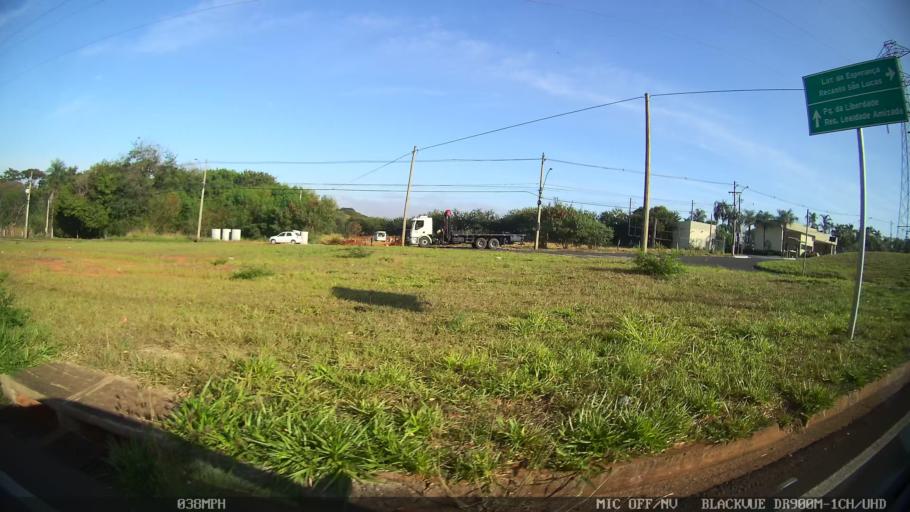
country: BR
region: Sao Paulo
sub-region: Sao Jose Do Rio Preto
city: Sao Jose do Rio Preto
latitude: -20.7831
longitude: -49.3430
